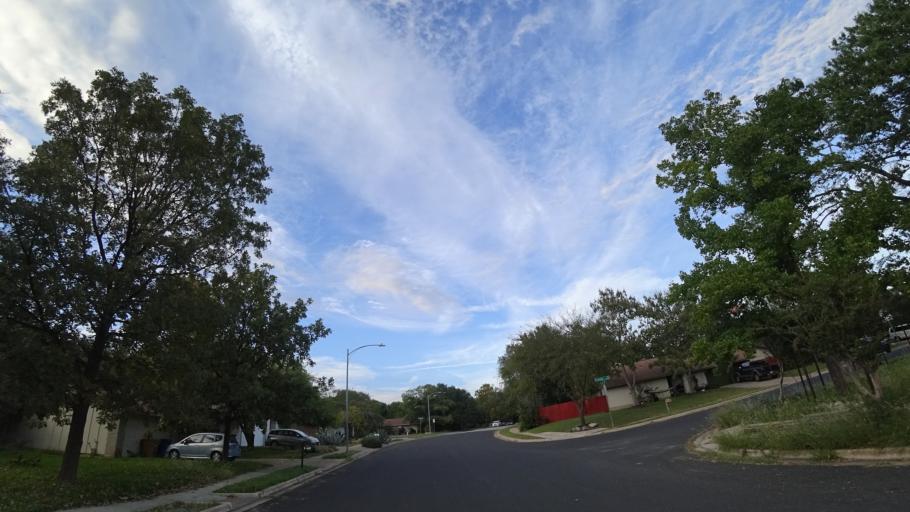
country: US
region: Texas
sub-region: Travis County
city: Austin
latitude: 30.2052
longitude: -97.7655
